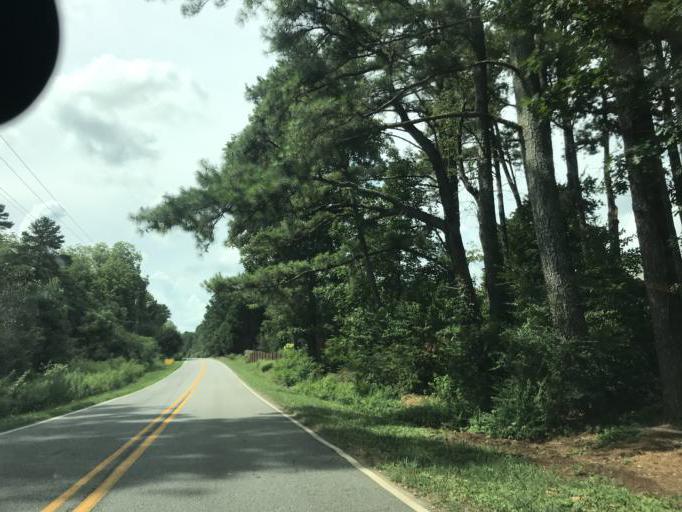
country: US
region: Georgia
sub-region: Forsyth County
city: Cumming
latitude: 34.2204
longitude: -84.2396
